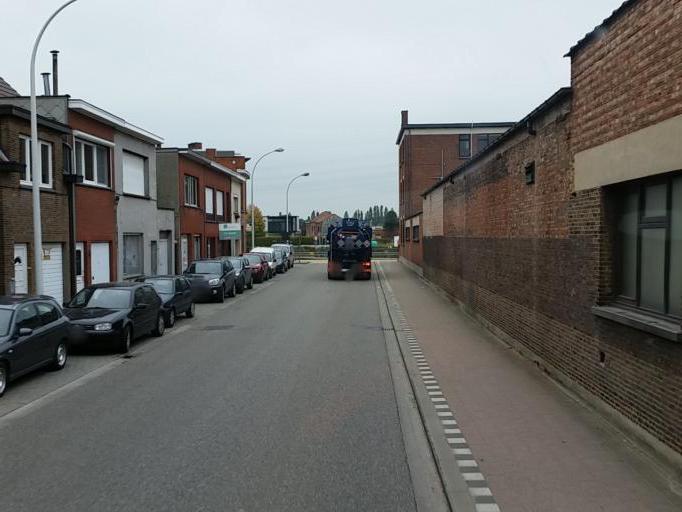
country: BE
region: Flanders
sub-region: Provincie Antwerpen
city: Schoten
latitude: 51.2408
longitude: 4.4741
